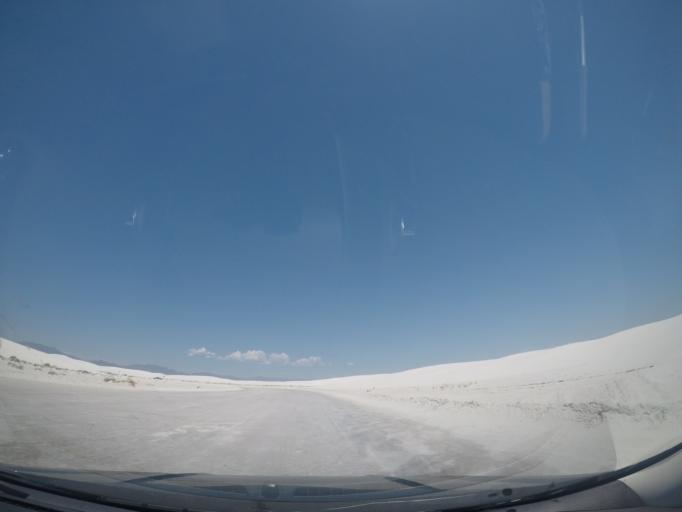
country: US
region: New Mexico
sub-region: Otero County
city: Holloman Air Force Base
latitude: 32.8229
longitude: -106.2703
